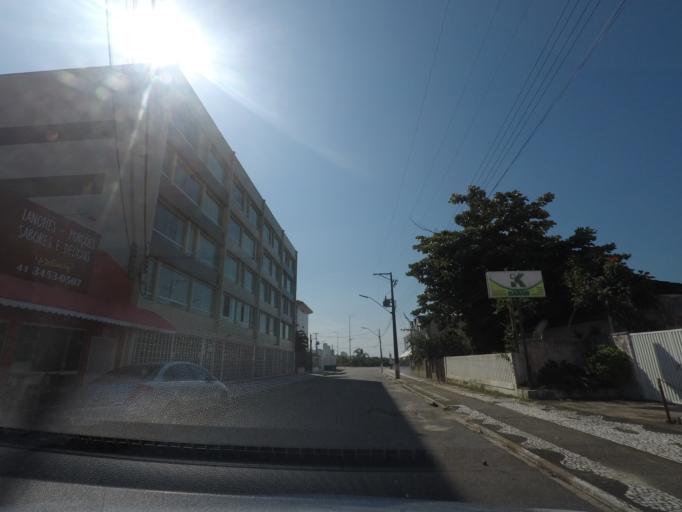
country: BR
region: Parana
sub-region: Guaratuba
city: Guaratuba
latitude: -25.8452
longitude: -48.5391
